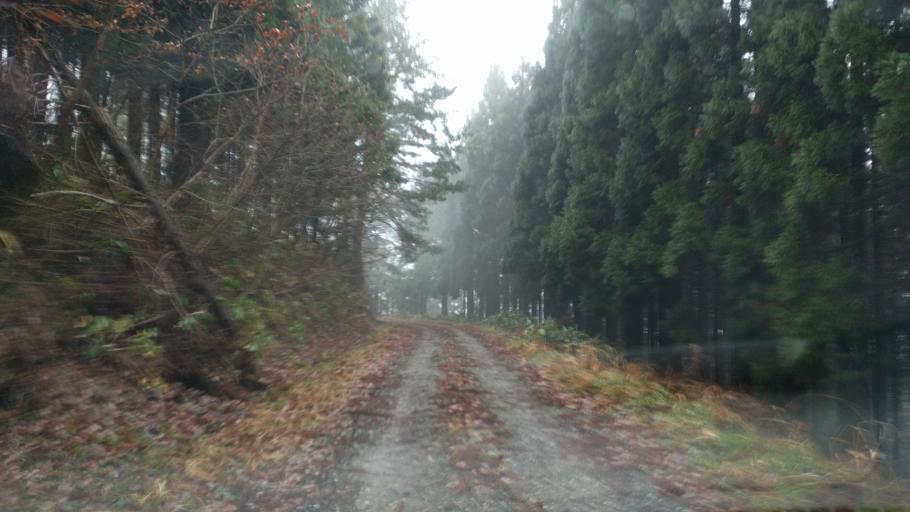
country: JP
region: Fukushima
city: Kitakata
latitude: 37.5758
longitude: 139.9736
